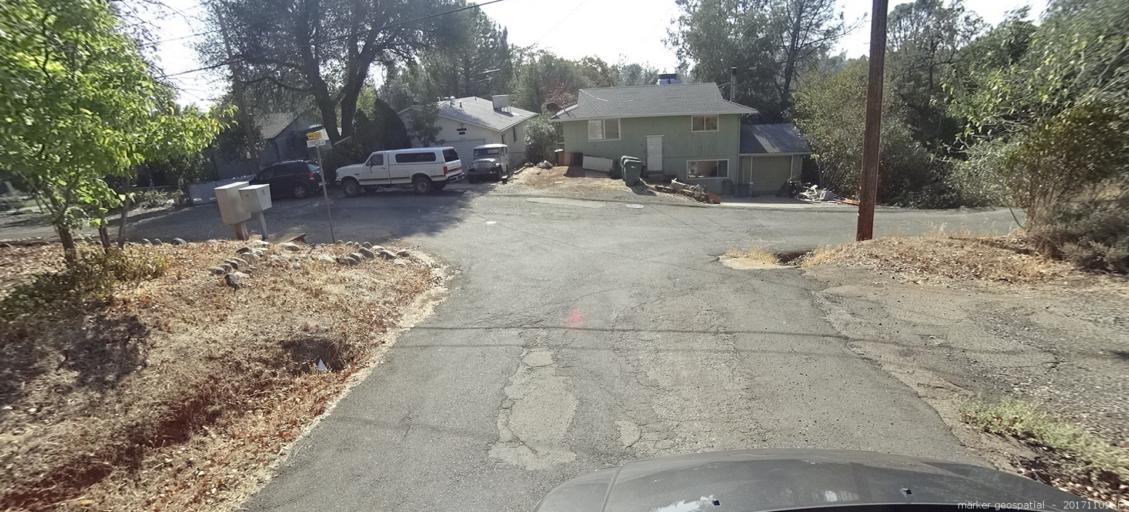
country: US
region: California
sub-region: Shasta County
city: Central Valley (historical)
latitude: 40.6851
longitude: -122.3761
